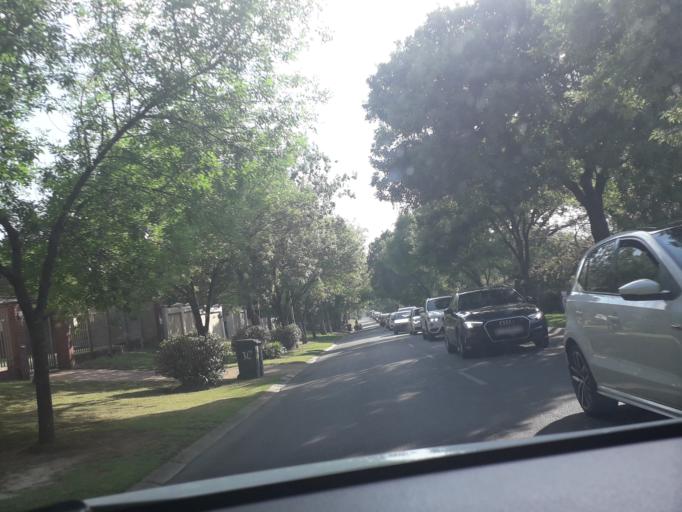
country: ZA
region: Gauteng
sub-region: City of Johannesburg Metropolitan Municipality
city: Diepsloot
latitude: -26.0567
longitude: 27.9793
